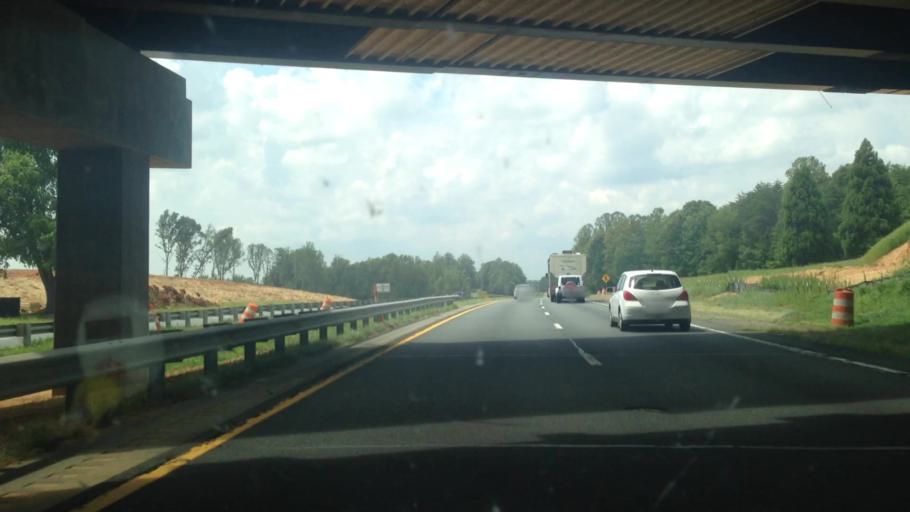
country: US
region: North Carolina
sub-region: Forsyth County
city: Rural Hall
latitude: 36.2107
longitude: -80.3032
